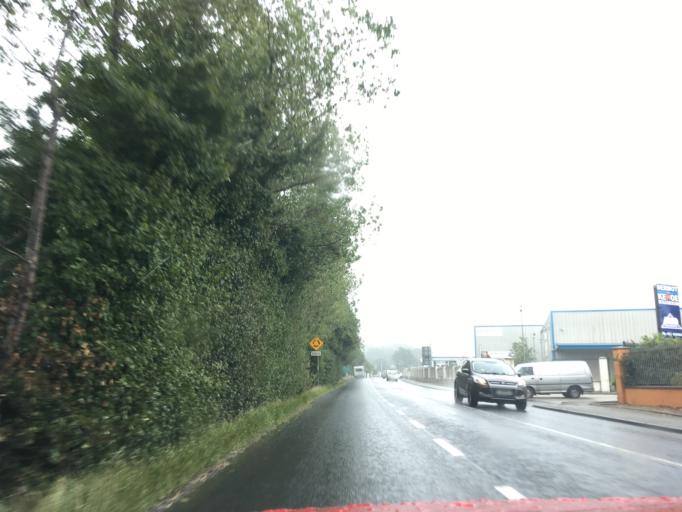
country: IE
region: Leinster
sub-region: Loch Garman
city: New Ross
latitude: 52.3885
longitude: -6.9281
